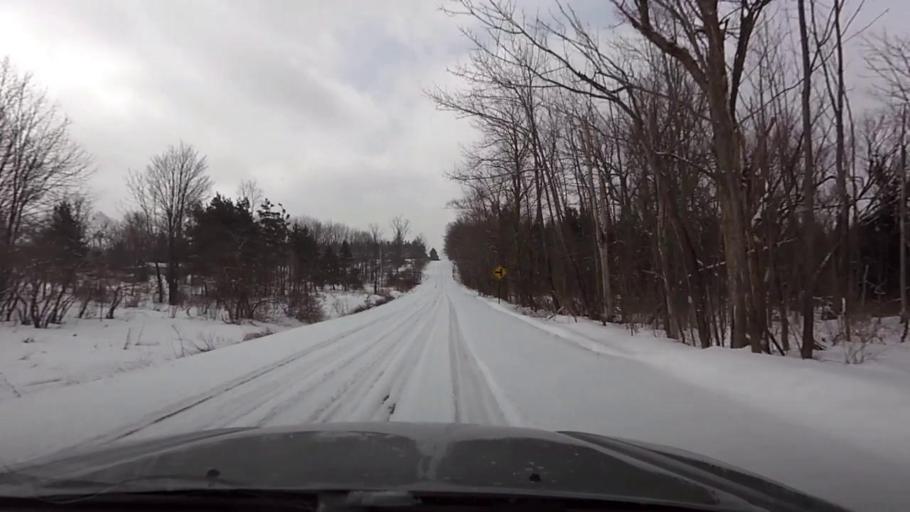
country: US
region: New York
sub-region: Cattaraugus County
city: Franklinville
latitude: 42.3222
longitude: -78.3540
